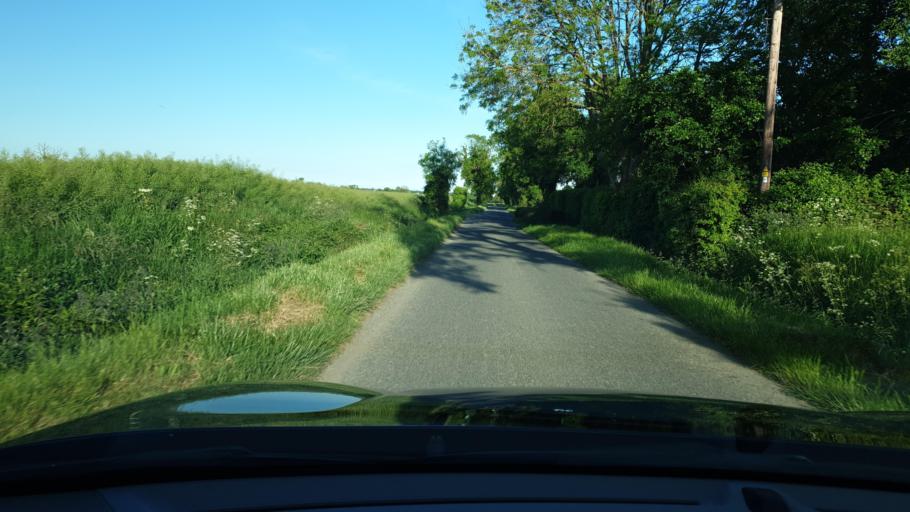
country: IE
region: Leinster
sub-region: Fingal County
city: Swords
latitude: 53.5029
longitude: -6.2391
